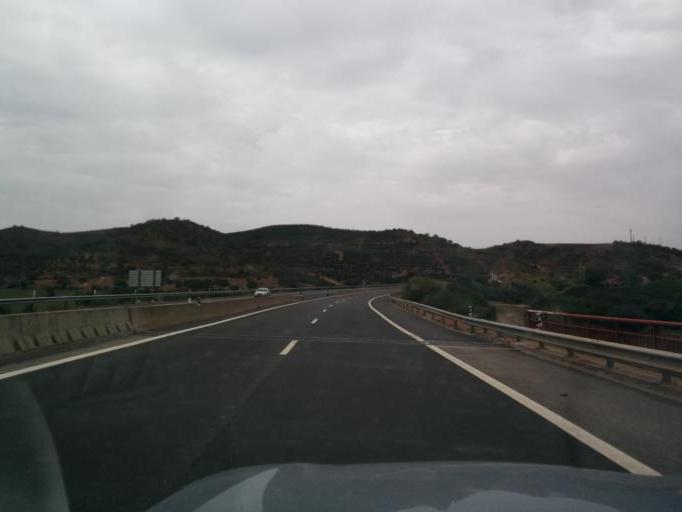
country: PT
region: Faro
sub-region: Tavira
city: Tavira
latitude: 37.1551
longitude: -7.6672
